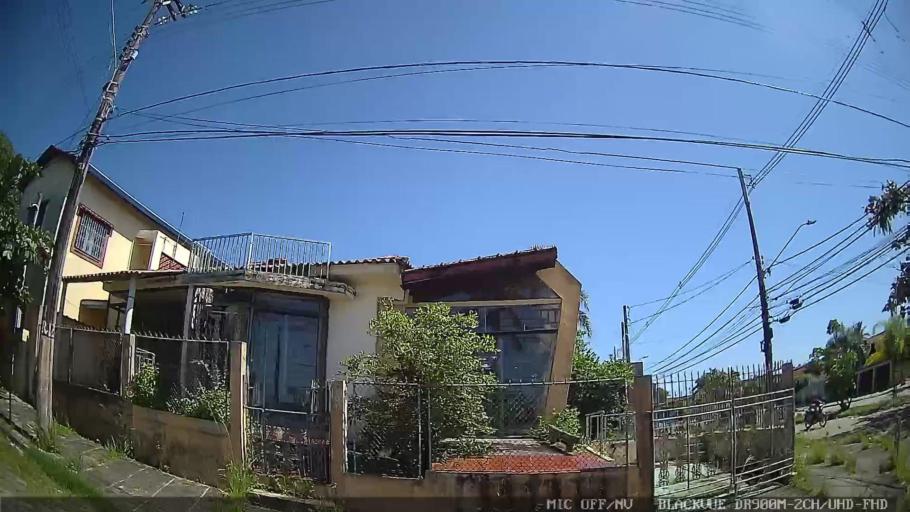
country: BR
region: Sao Paulo
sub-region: Peruibe
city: Peruibe
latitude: -24.3038
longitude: -46.9827
